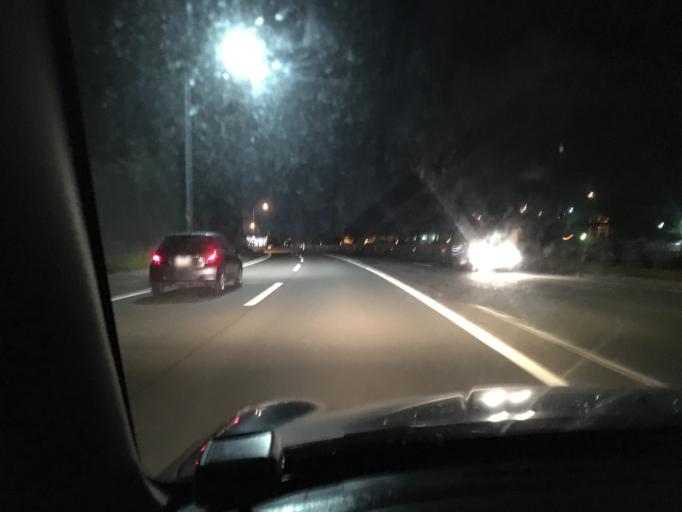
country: JP
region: Hokkaido
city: Muroran
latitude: 42.3535
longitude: 140.9954
